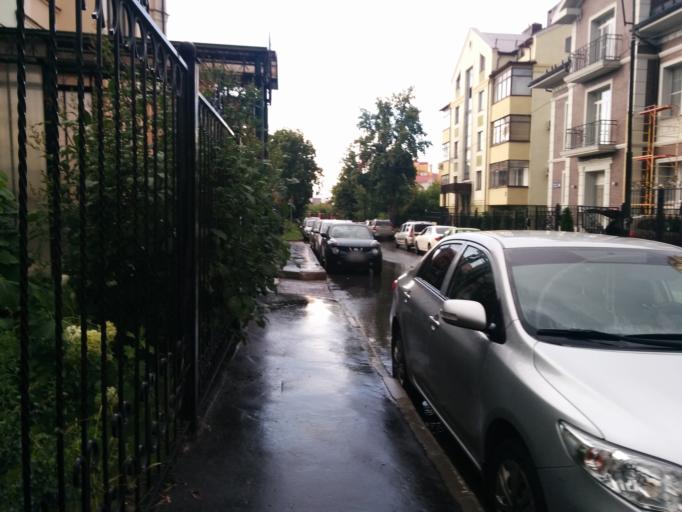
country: RU
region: Tatarstan
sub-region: Gorod Kazan'
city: Kazan
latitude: 55.8000
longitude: 49.1215
